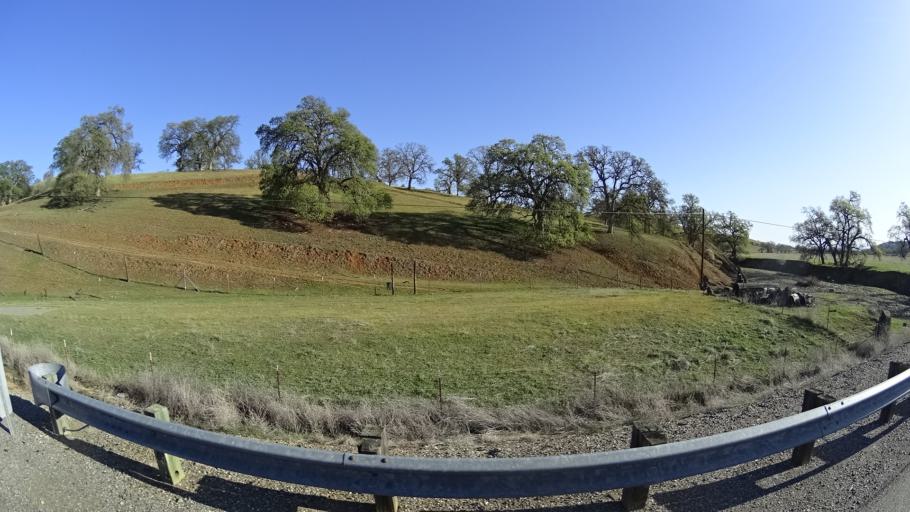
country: US
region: California
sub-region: Tehama County
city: Rancho Tehama Reserve
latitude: 39.7856
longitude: -122.4766
